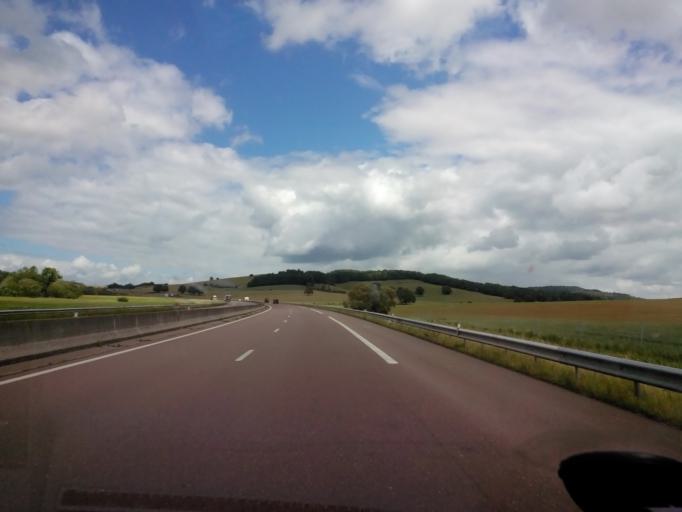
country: FR
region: Lorraine
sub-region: Departement des Vosges
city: Chatenois
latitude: 48.3541
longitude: 5.8620
